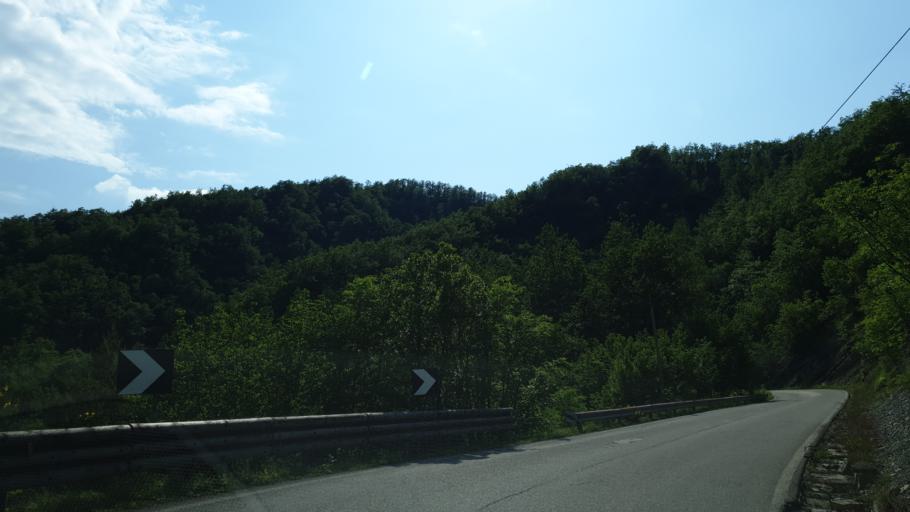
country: IT
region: Emilia-Romagna
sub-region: Forli-Cesena
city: San Piero in Bagno
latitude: 43.8189
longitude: 11.9543
